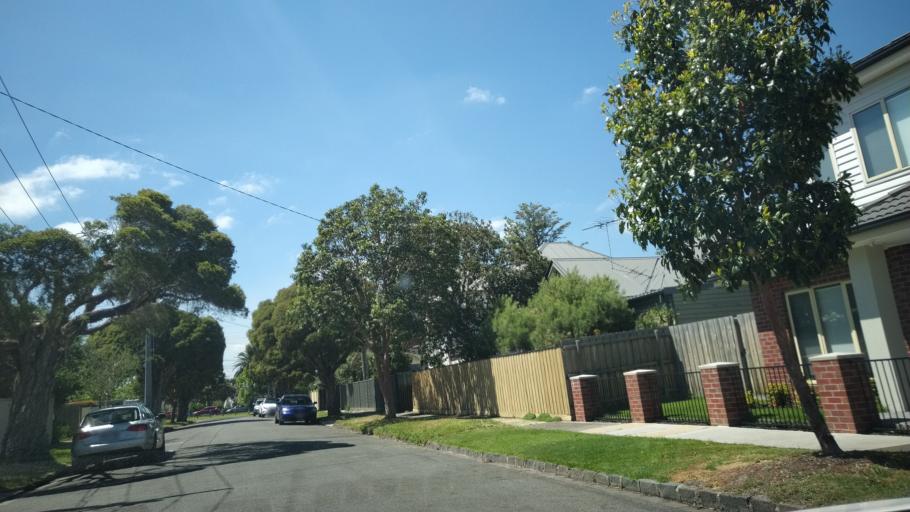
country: AU
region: Victoria
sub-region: Glen Eira
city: Glen Huntly
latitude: -37.8924
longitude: 145.0403
